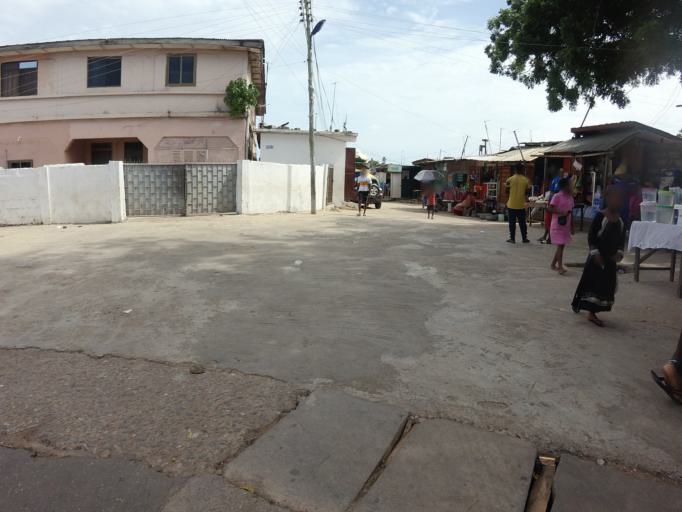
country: GH
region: Greater Accra
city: Accra
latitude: 5.5848
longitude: -0.2036
